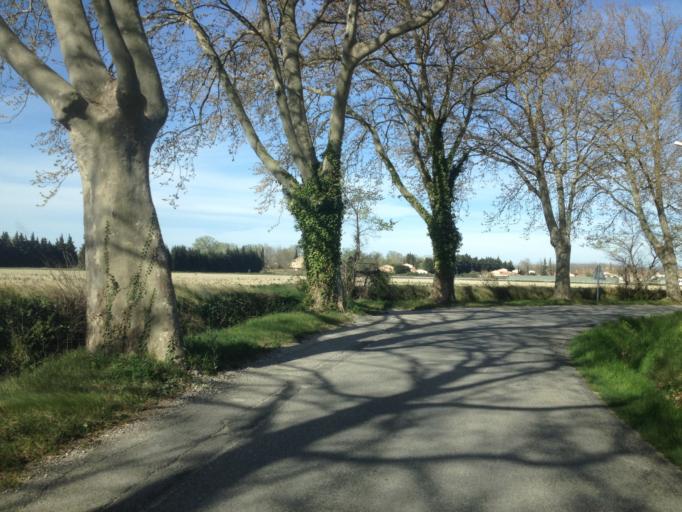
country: FR
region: Provence-Alpes-Cote d'Azur
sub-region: Departement du Vaucluse
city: Caderousse
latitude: 44.0990
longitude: 4.7651
